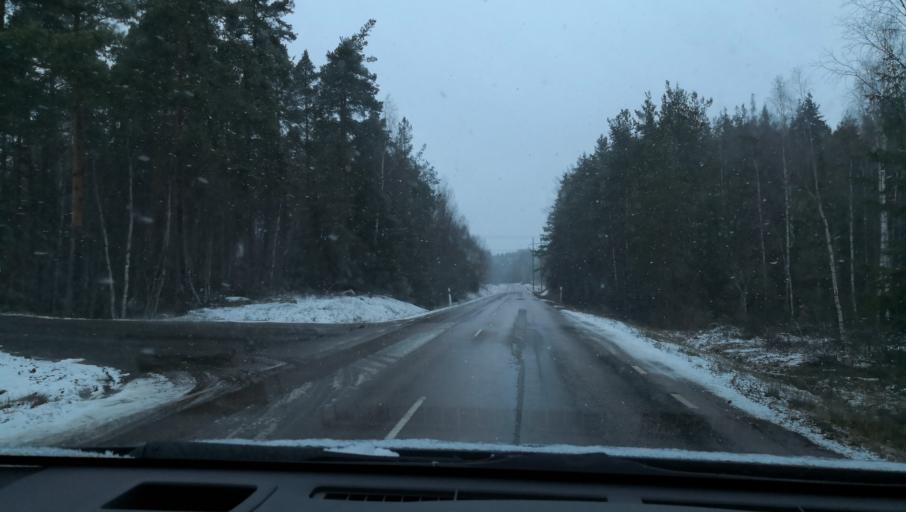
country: SE
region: Vaestmanland
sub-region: Hallstahammars Kommun
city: Kolback
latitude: 59.5838
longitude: 16.3553
